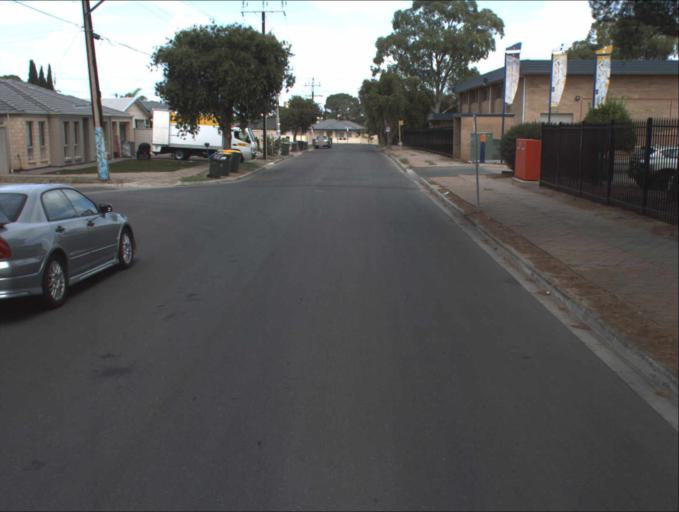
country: AU
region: South Australia
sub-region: Port Adelaide Enfield
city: Gilles Plains
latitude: -34.8620
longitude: 138.6586
